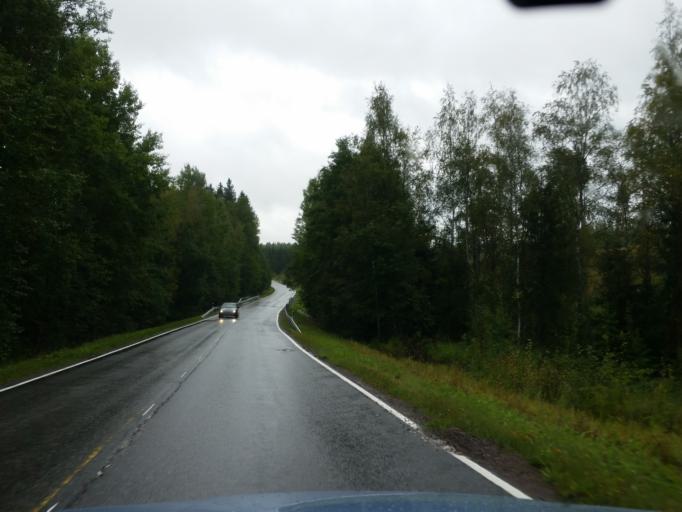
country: FI
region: Uusimaa
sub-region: Helsinki
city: Sammatti
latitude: 60.3853
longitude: 23.8001
